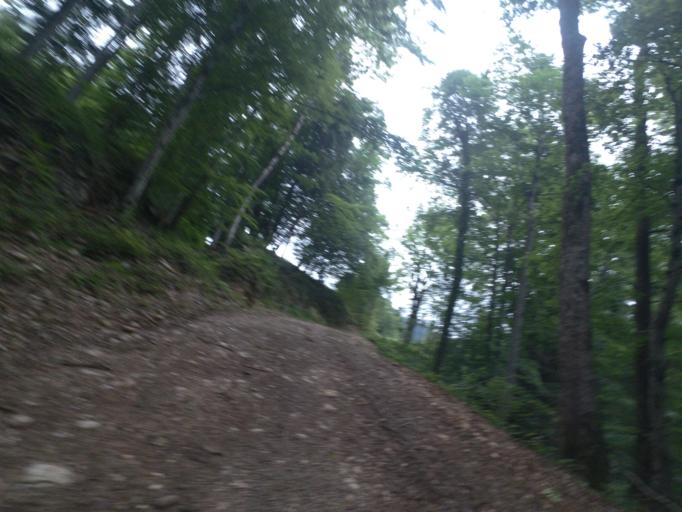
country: AT
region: Salzburg
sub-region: Politischer Bezirk Salzburg-Umgebung
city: Elsbethen
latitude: 47.7690
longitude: 13.0996
